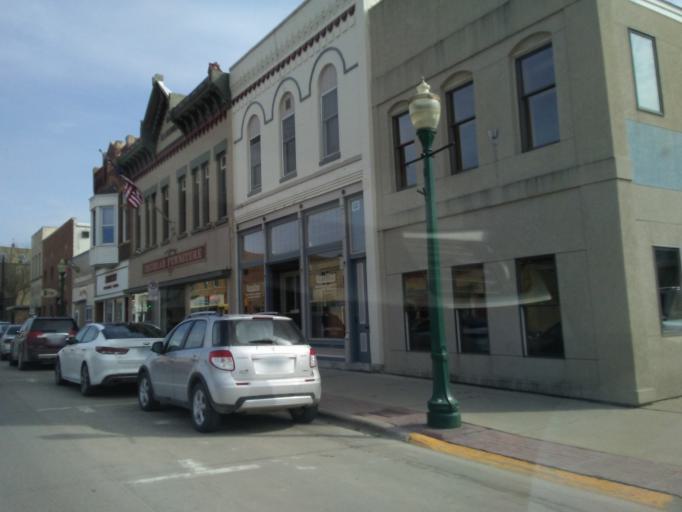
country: US
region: Iowa
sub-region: Winneshiek County
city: Decorah
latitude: 43.3041
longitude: -91.7894
